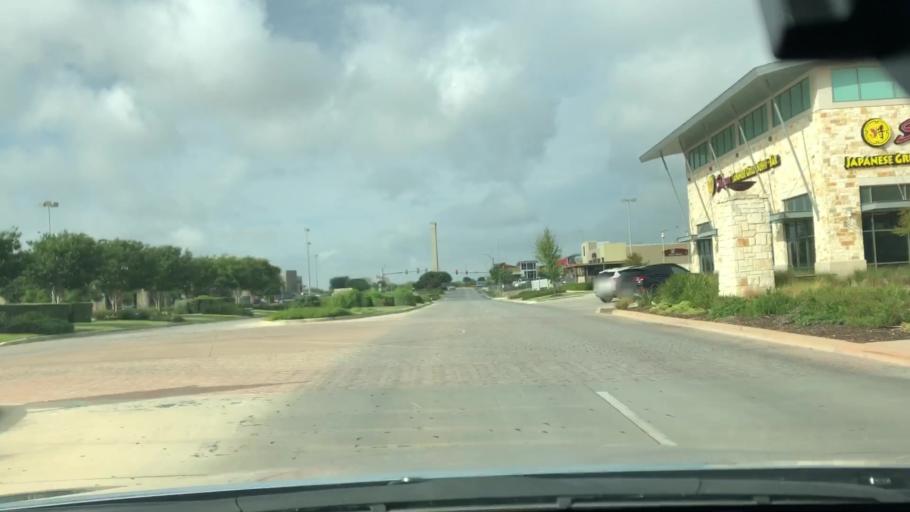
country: US
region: Texas
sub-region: Guadalupe County
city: Lake Dunlap
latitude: 29.7287
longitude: -98.0739
